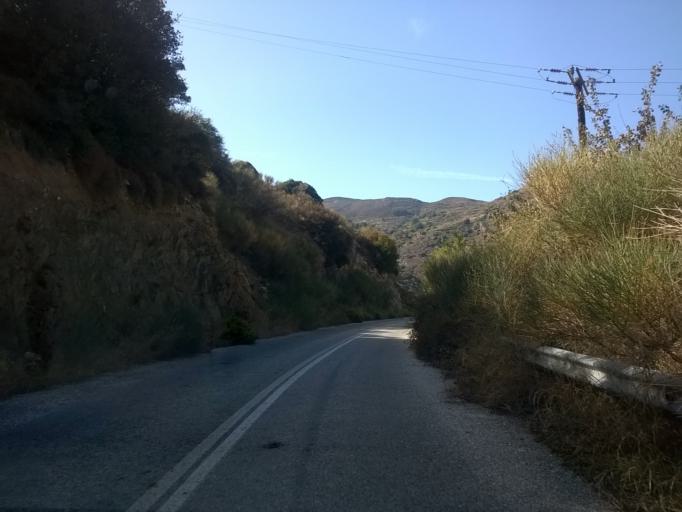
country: GR
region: South Aegean
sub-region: Nomos Kykladon
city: Filotion
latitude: 37.1458
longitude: 25.5455
